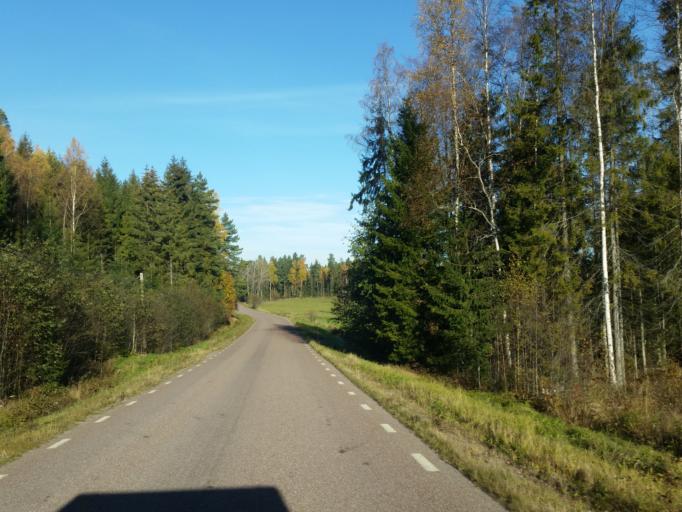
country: SE
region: Dalarna
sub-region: Borlange Kommun
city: Ornas
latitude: 60.4558
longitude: 15.6170
